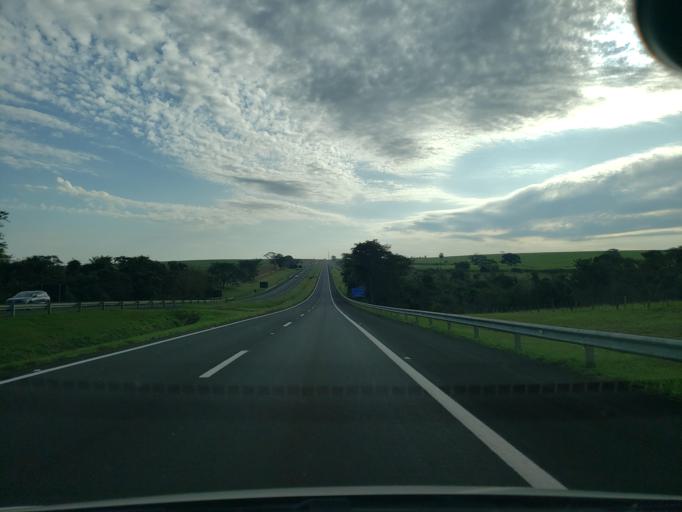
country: BR
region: Sao Paulo
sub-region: Guararapes
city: Guararapes
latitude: -21.2095
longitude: -50.7395
